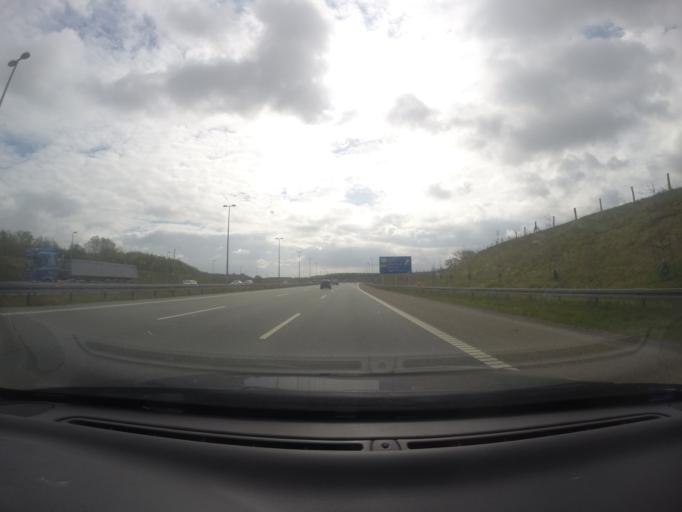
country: DK
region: Capital Region
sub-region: Glostrup Kommune
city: Glostrup
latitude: 55.6944
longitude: 12.3969
